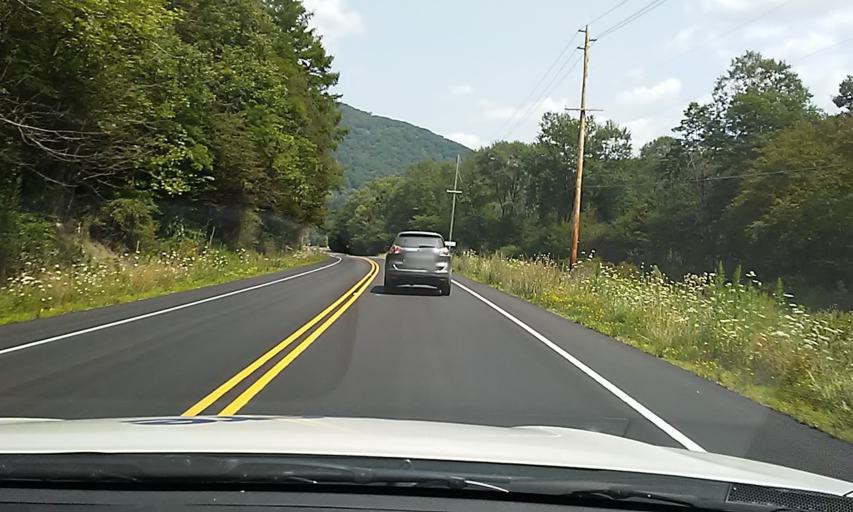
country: US
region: Pennsylvania
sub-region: Cameron County
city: Emporium
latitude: 41.4754
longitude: -78.3741
